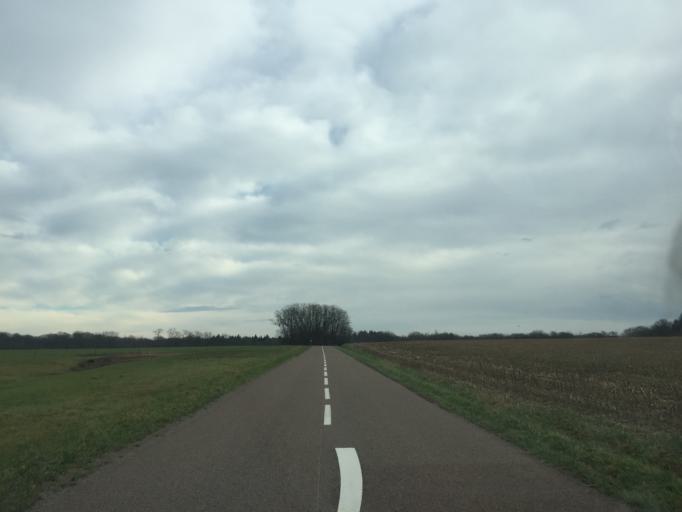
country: FR
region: Franche-Comte
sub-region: Departement du Jura
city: Chaussin
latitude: 46.9217
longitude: 5.4902
